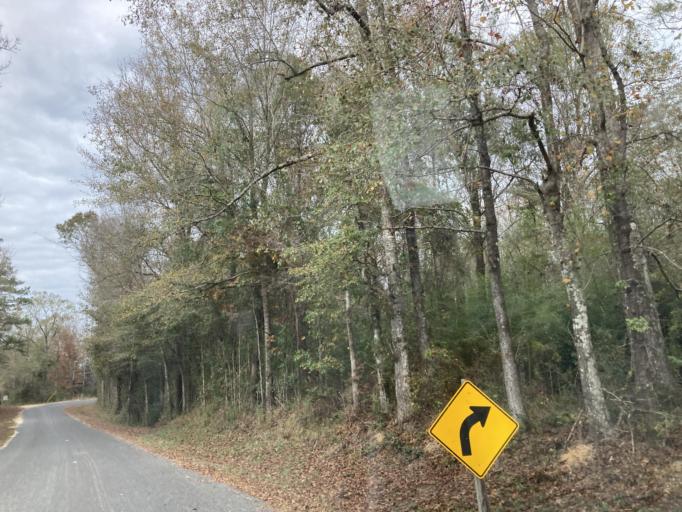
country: US
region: Mississippi
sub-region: Perry County
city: New Augusta
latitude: 31.0726
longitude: -89.1662
